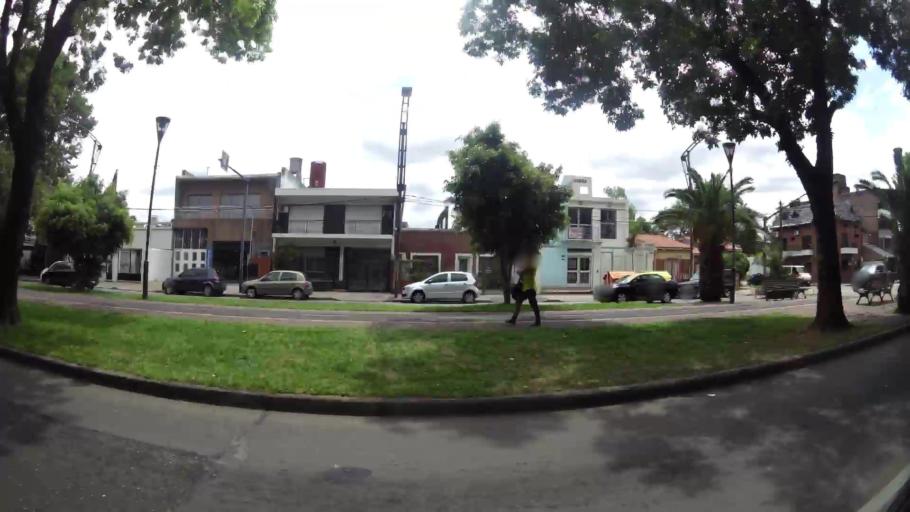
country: AR
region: Santa Fe
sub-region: Departamento de Rosario
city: Rosario
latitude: -32.9675
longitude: -60.6593
